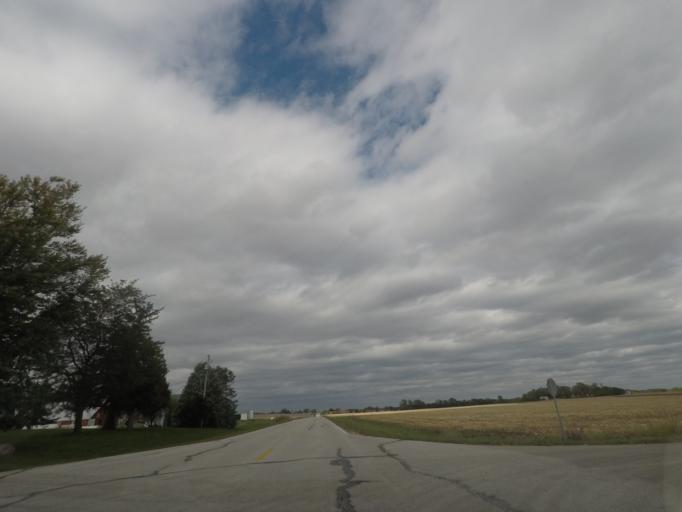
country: US
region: Iowa
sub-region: Story County
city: Huxley
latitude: 41.8494
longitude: -93.5315
